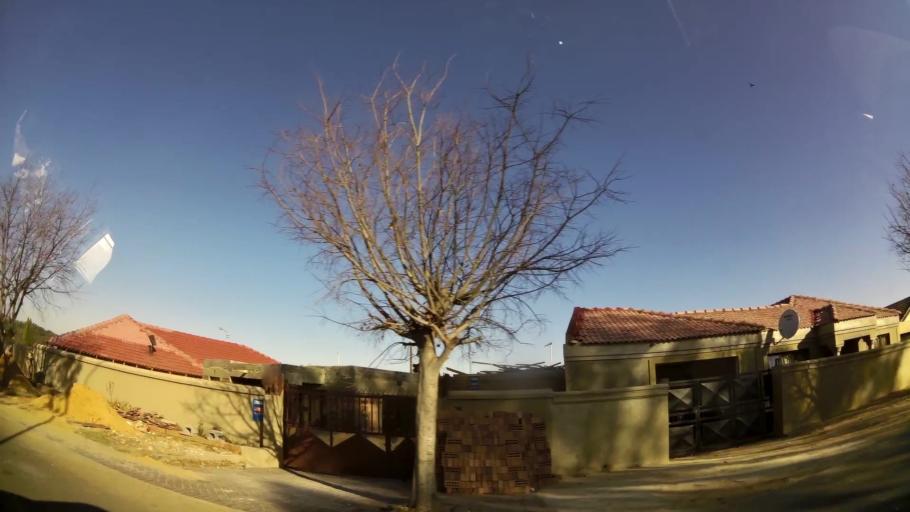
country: ZA
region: Gauteng
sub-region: City of Johannesburg Metropolitan Municipality
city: Johannesburg
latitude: -26.2168
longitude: 27.9852
